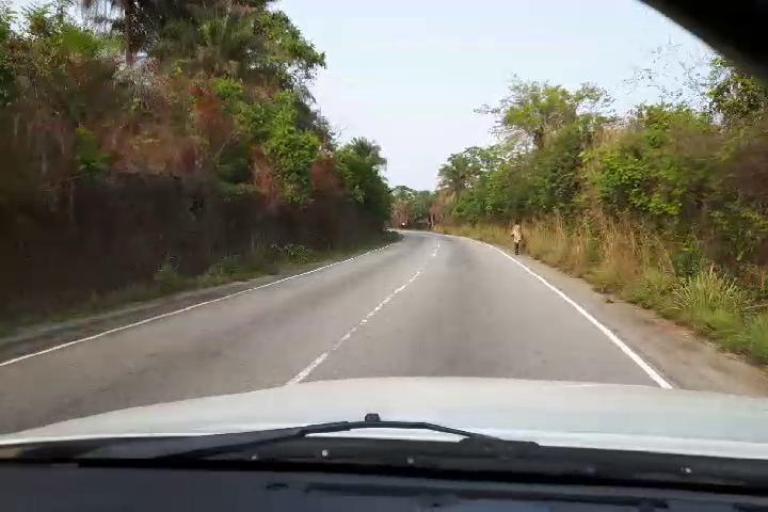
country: SL
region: Southern Province
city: Baoma
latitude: 7.9275
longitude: -11.5334
